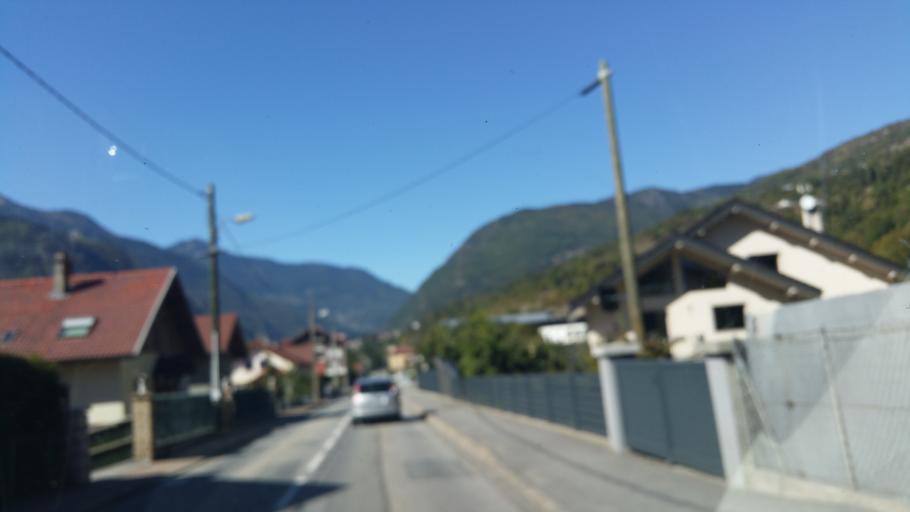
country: FR
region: Rhone-Alpes
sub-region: Departement de la Savoie
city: Aigueblanche
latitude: 45.5027
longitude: 6.5078
